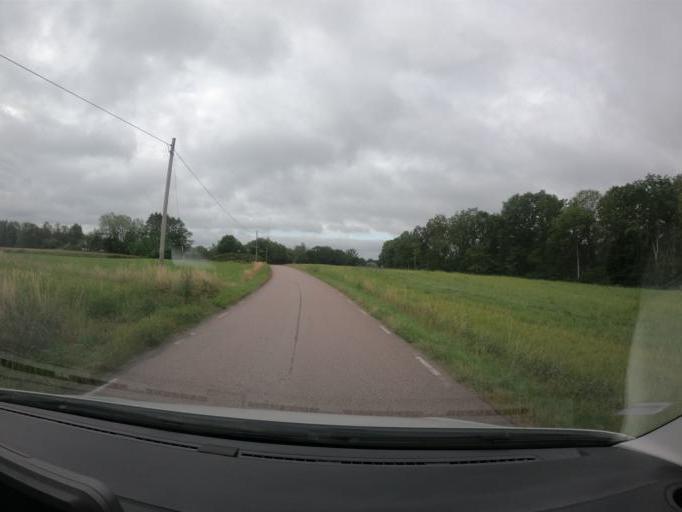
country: SE
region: Skane
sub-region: Angelholms Kommun
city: Munka-Ljungby
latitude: 56.3402
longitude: 12.9721
